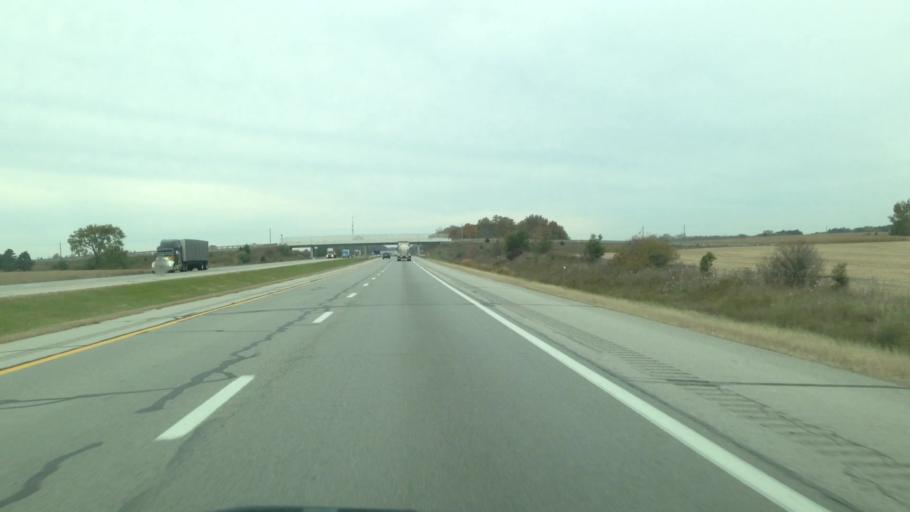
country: US
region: Ohio
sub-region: Williams County
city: West Unity
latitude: 41.6069
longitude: -84.4738
